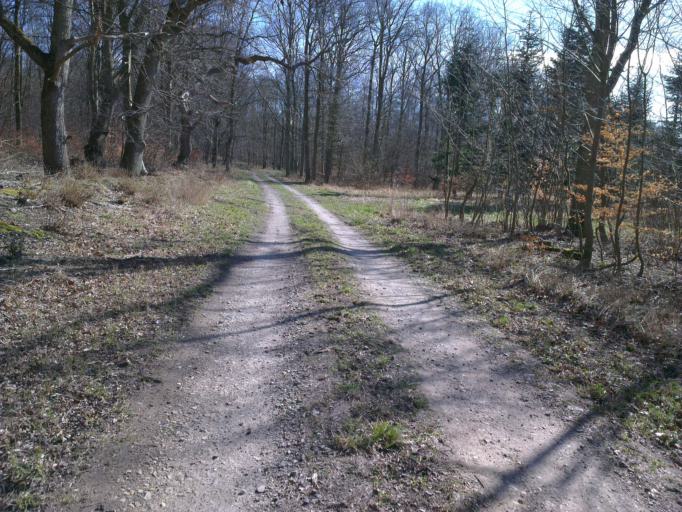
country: DK
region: Capital Region
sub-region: Frederikssund Kommune
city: Jaegerspris
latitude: 55.8909
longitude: 11.9973
